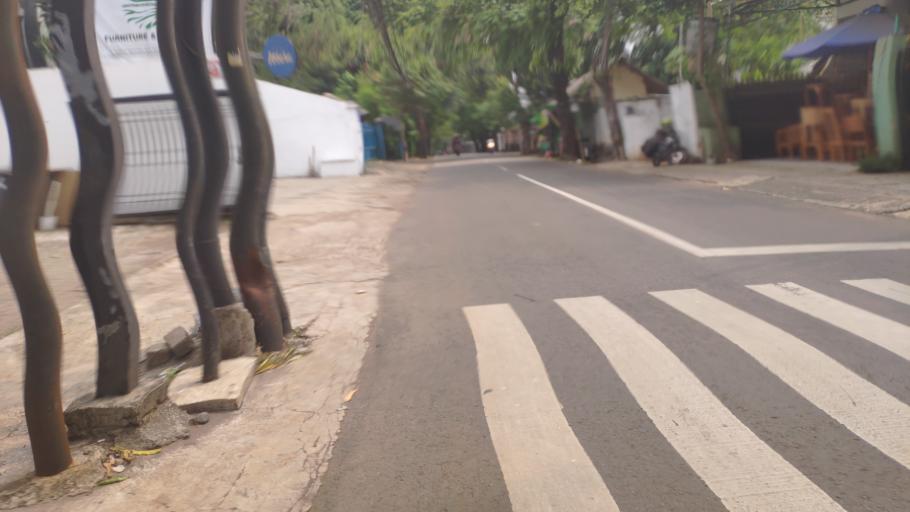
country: ID
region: Jakarta Raya
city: Jakarta
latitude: -6.2607
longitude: 106.8234
